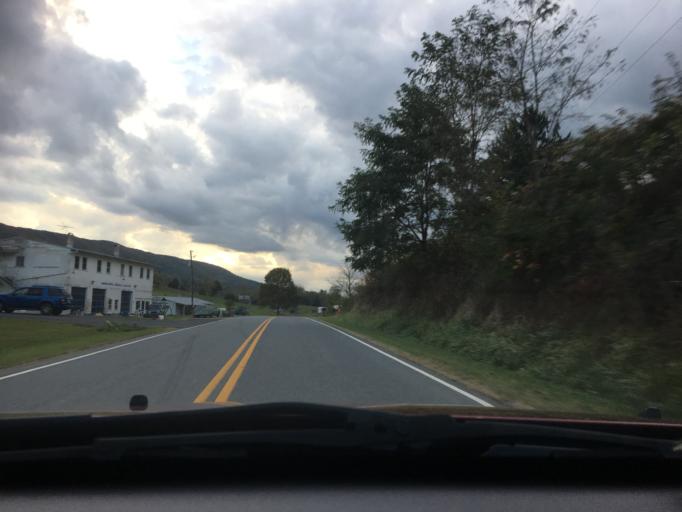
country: US
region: Virginia
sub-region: Giles County
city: Pearisburg
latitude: 37.2146
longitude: -80.7602
